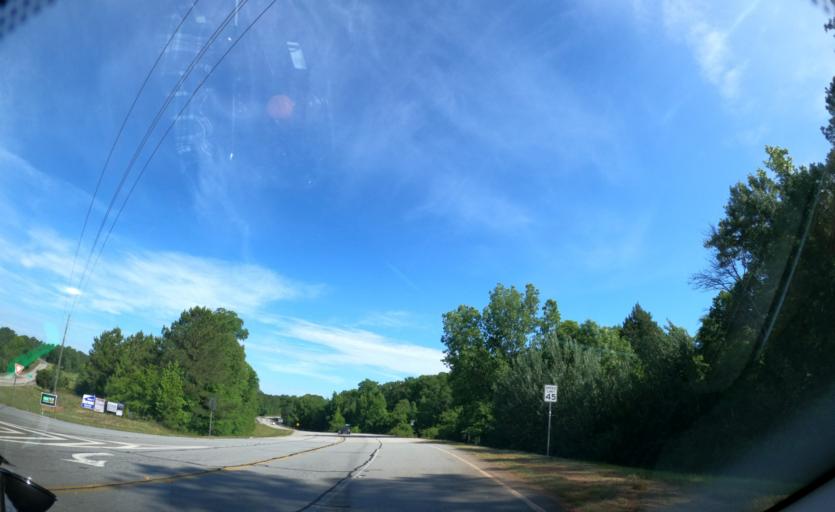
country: US
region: Georgia
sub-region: Lincoln County
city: Lincolnton
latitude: 33.7872
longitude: -82.4374
